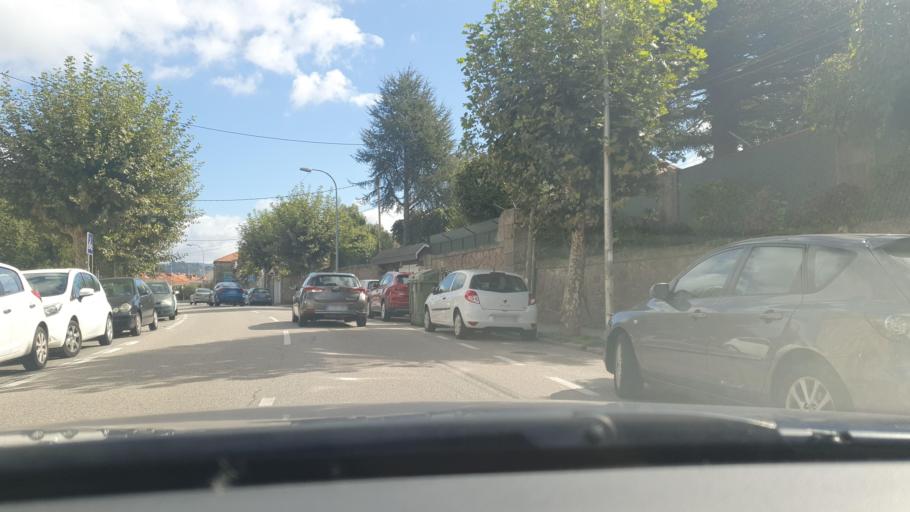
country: ES
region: Galicia
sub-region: Provincia de Pontevedra
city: Vigo
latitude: 42.2216
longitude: -8.7589
